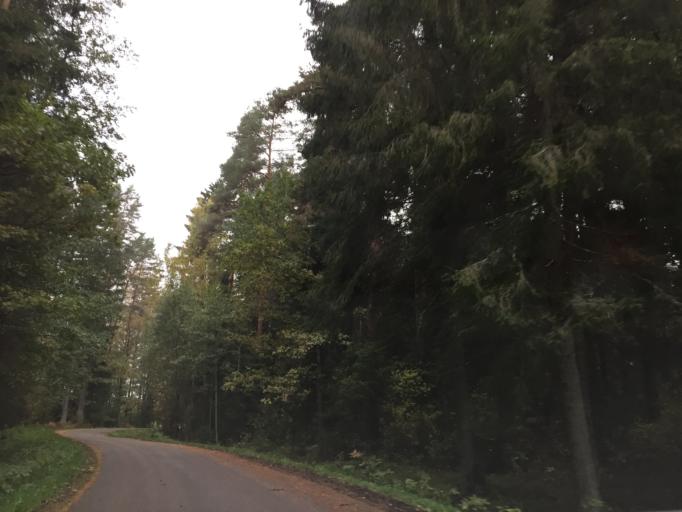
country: LV
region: Jelgava
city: Jelgava
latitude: 56.7333
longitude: 23.6877
